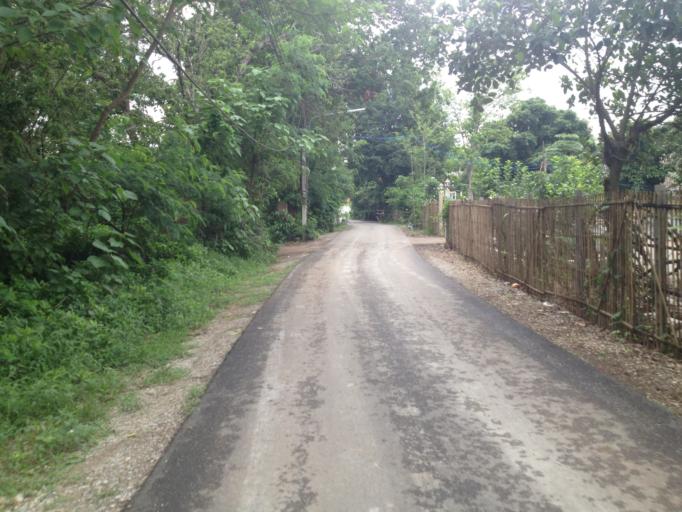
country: TH
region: Chiang Mai
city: Hang Dong
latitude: 18.7157
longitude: 98.9068
